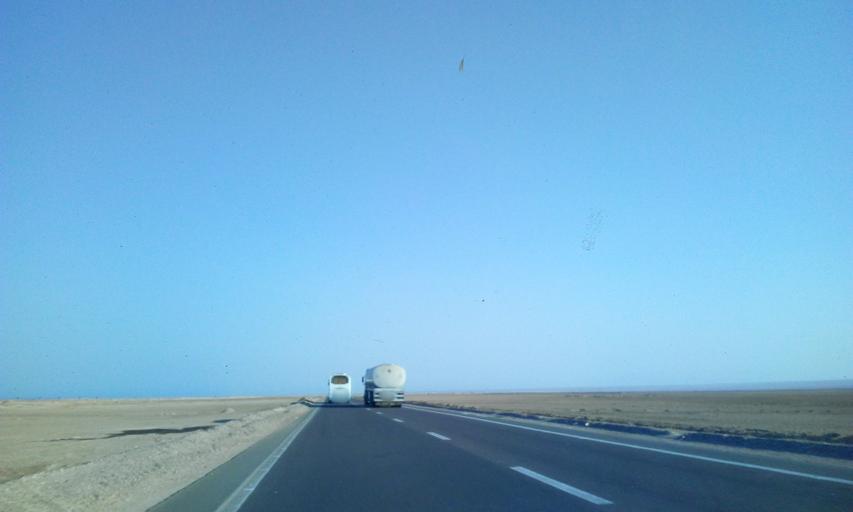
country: EG
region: South Sinai
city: Tor
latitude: 28.6467
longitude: 32.8500
